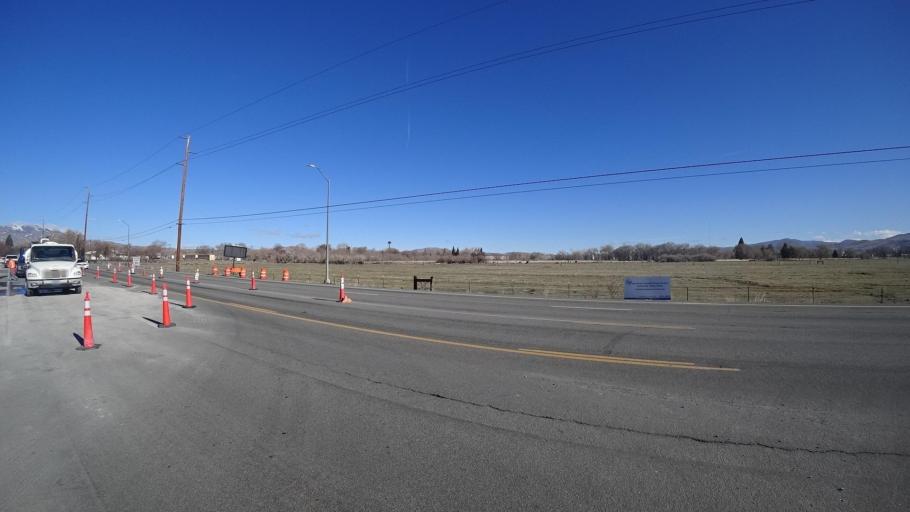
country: US
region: Nevada
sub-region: Washoe County
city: Sparks
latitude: 39.5127
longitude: -119.7476
